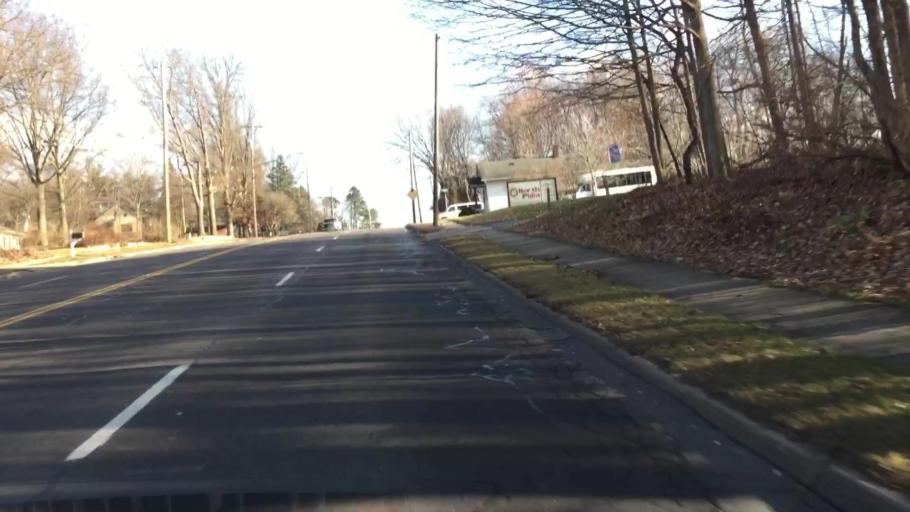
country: US
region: Ohio
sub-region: Portage County
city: Kent
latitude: 41.1540
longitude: -81.3951
